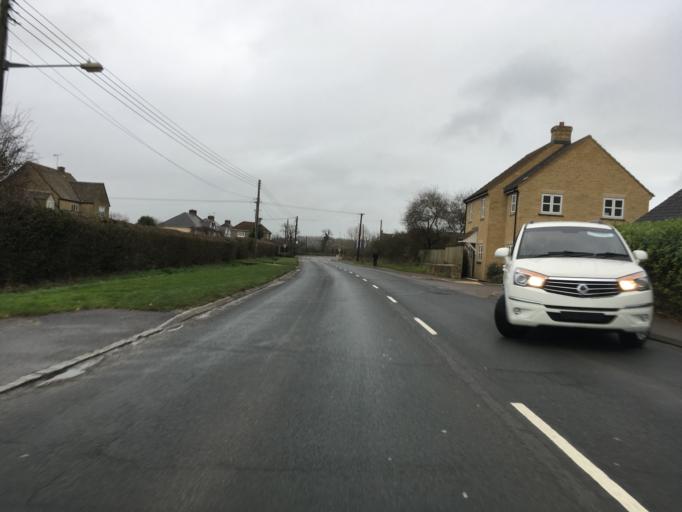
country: GB
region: England
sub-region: Wiltshire
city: Malmesbury
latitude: 51.5970
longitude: -2.0999
